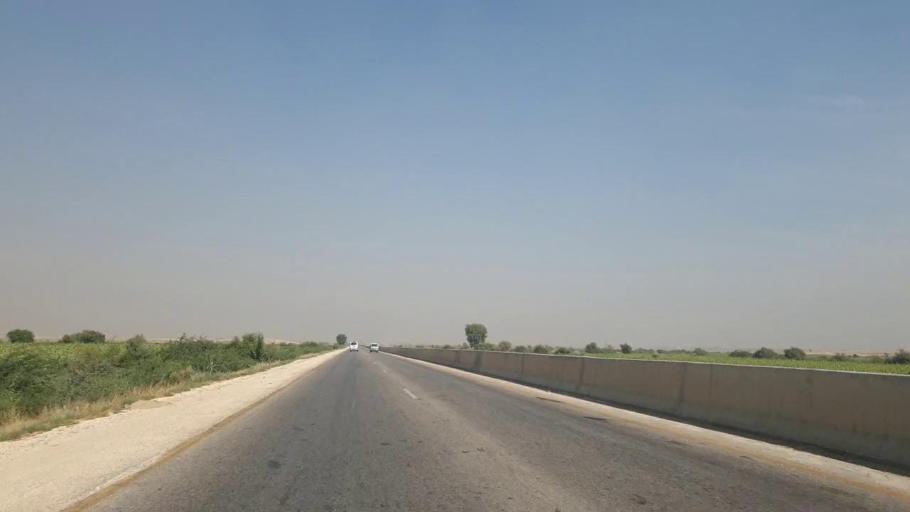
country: PK
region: Sindh
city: Jamshoro
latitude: 25.5467
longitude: 68.2937
